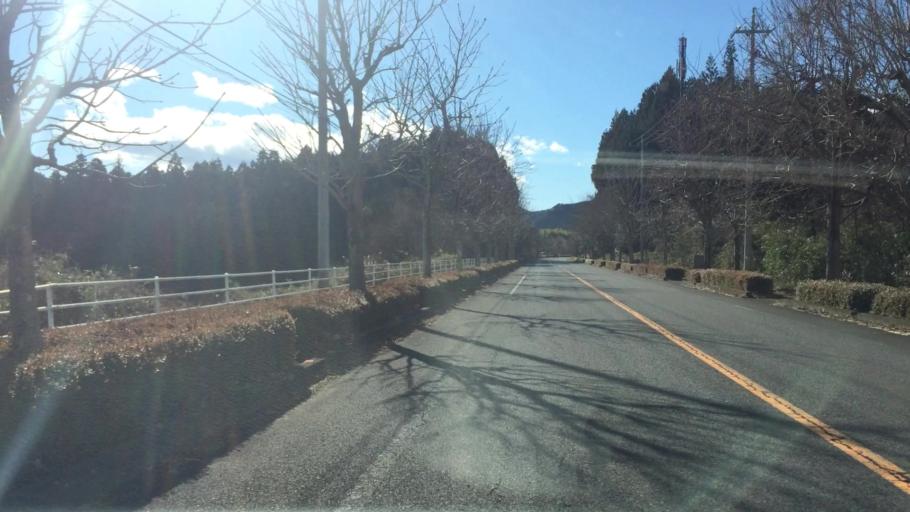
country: JP
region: Tochigi
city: Imaichi
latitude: 36.8062
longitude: 139.7067
